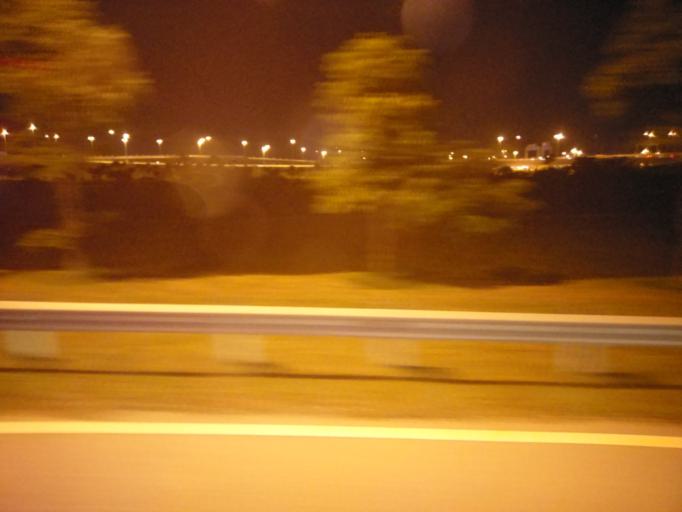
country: MY
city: Sungai Pelek New Village
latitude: 2.7505
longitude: 101.6878
